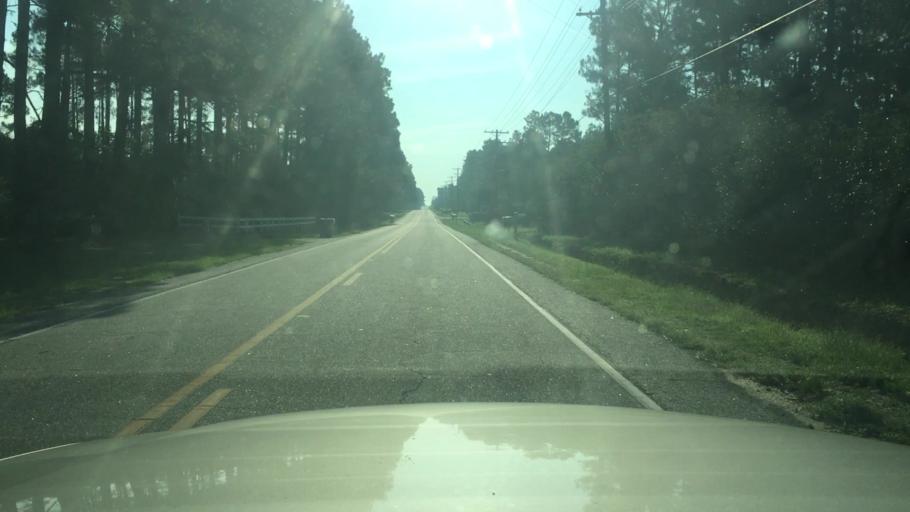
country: US
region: North Carolina
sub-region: Cumberland County
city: Spring Lake
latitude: 35.2065
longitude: -78.8834
